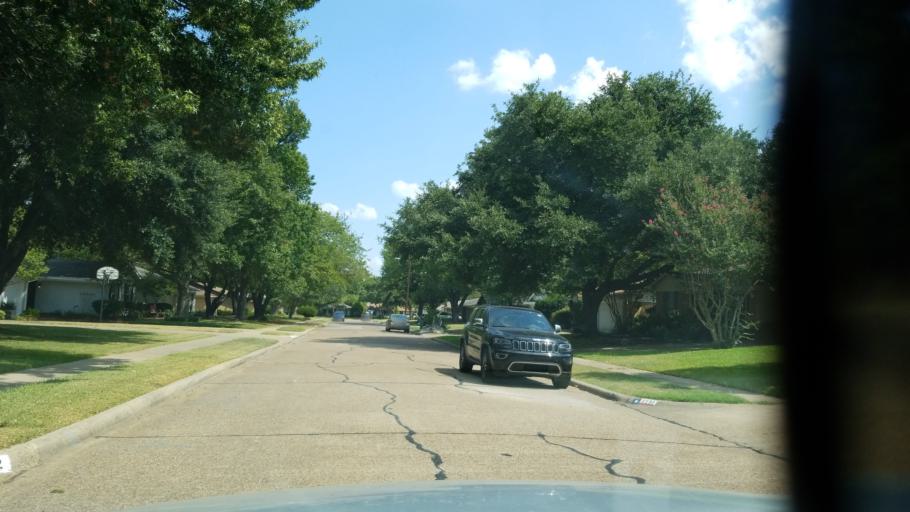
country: US
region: Texas
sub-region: Dallas County
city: Richardson
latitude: 32.9600
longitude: -96.7614
